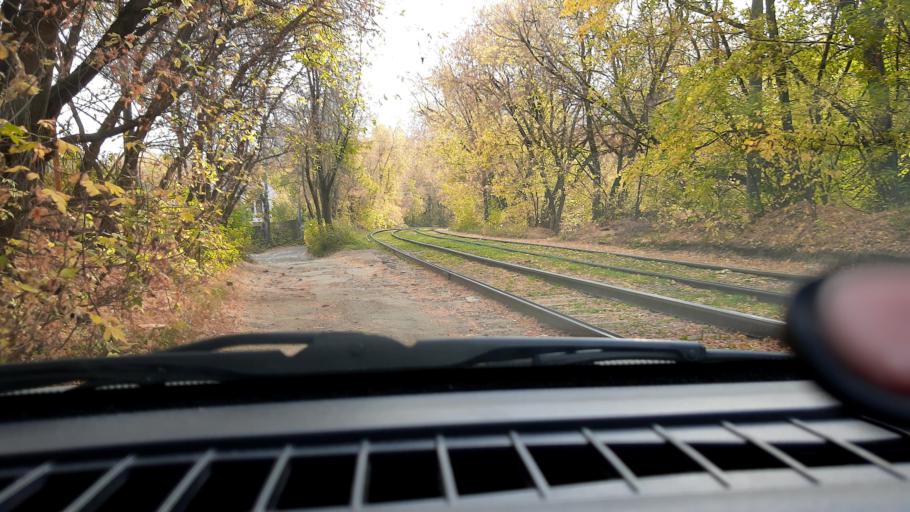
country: RU
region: Nizjnij Novgorod
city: Nizhniy Novgorod
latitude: 56.2959
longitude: 43.9927
